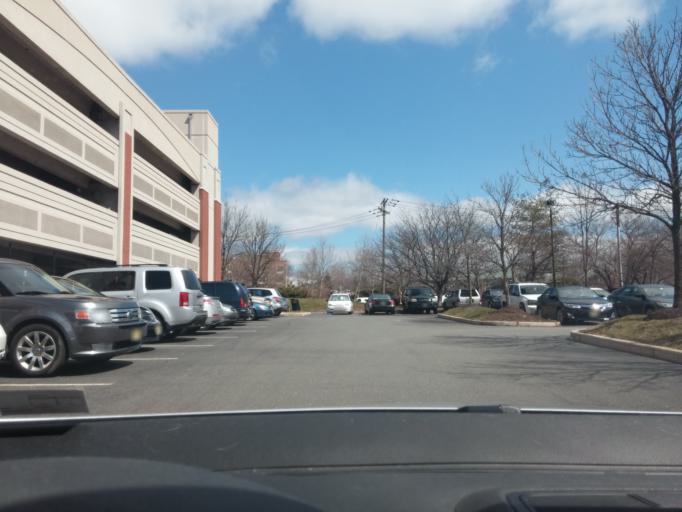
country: US
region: New Jersey
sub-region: Mercer County
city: Trenton
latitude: 40.2059
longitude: -74.7626
